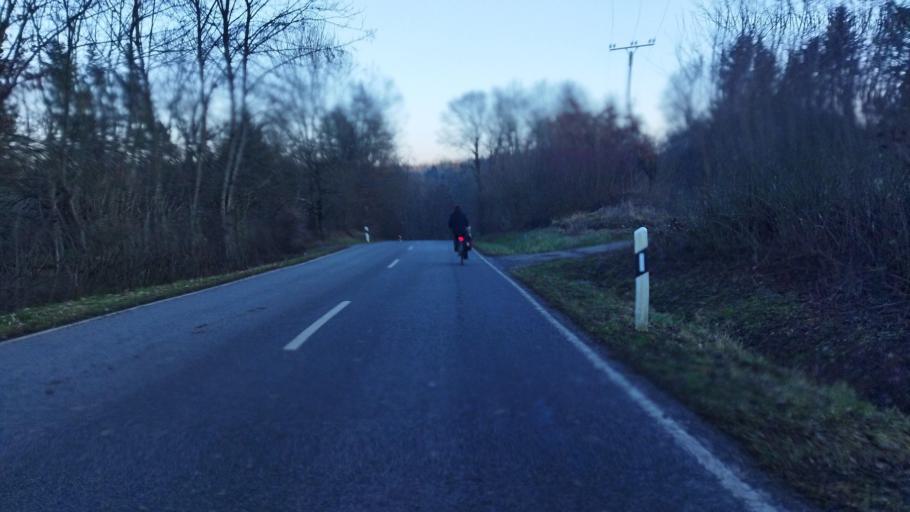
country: DE
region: Baden-Wuerttemberg
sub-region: Regierungsbezirk Stuttgart
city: Talheim
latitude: 49.0666
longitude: 9.2015
